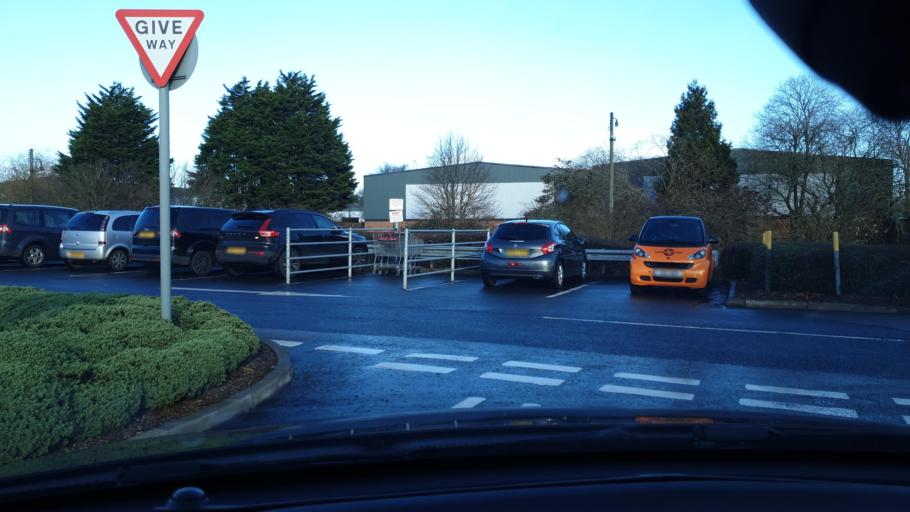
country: GB
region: England
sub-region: City and Borough of Birmingham
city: Birmingham
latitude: 52.5025
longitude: -1.8518
